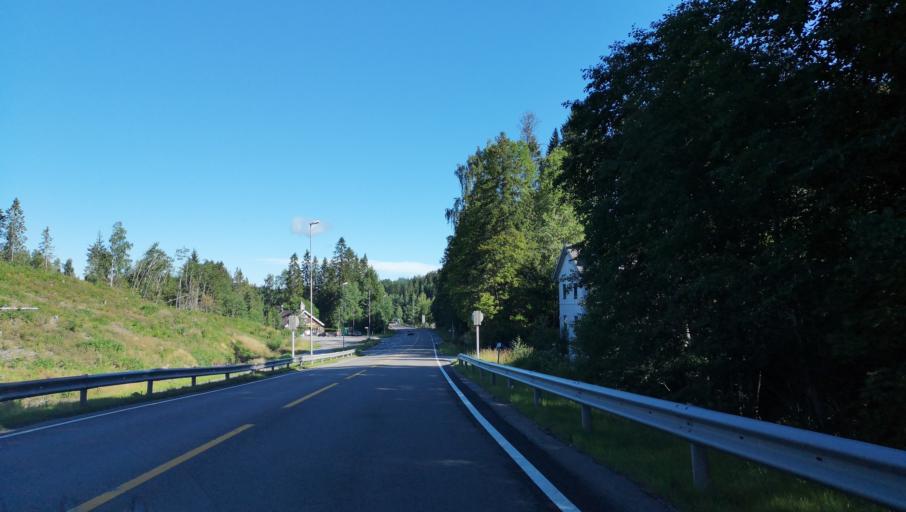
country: NO
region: Ostfold
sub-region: Spydeberg
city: Spydeberg
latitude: 59.5990
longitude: 11.1032
